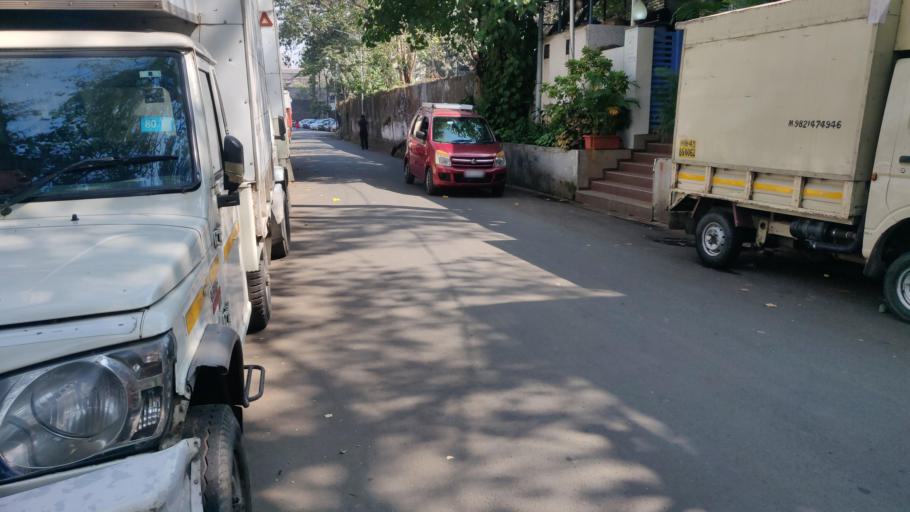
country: IN
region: Maharashtra
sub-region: Mumbai Suburban
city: Mumbai
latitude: 18.9829
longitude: 72.8380
